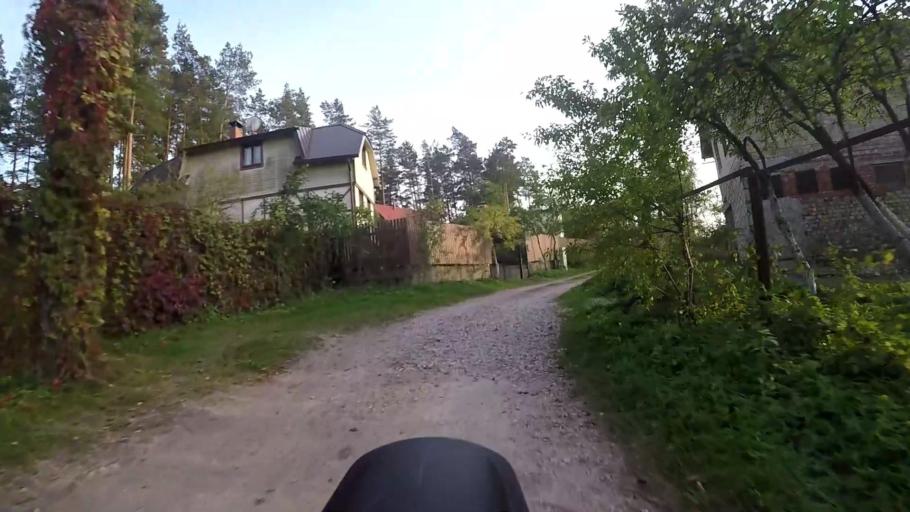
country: LV
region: Saulkrastu
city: Saulkrasti
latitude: 57.1903
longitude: 24.3535
